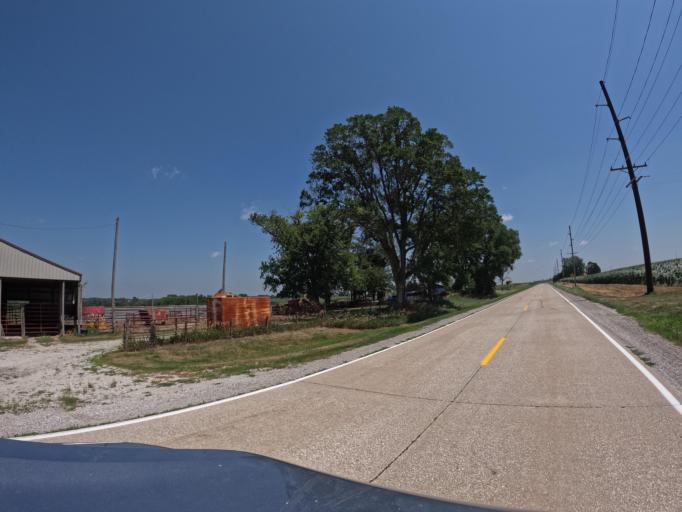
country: US
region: Iowa
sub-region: Keokuk County
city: Sigourney
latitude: 41.2757
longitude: -92.1656
